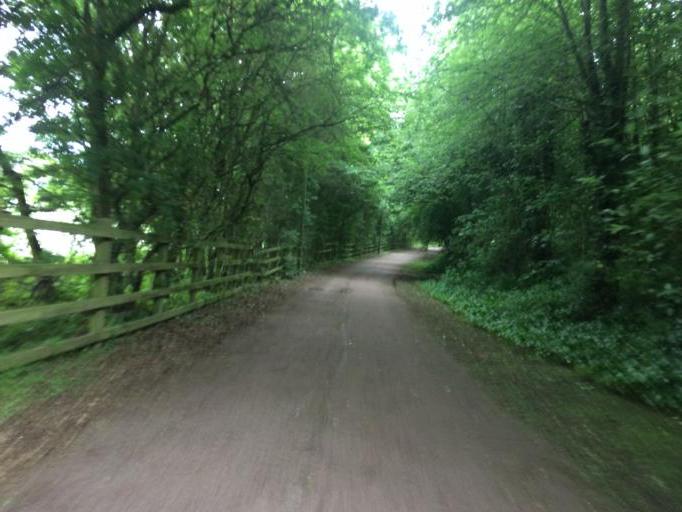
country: GB
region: England
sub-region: Milton Keynes
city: Loughton
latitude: 52.0316
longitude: -0.7730
